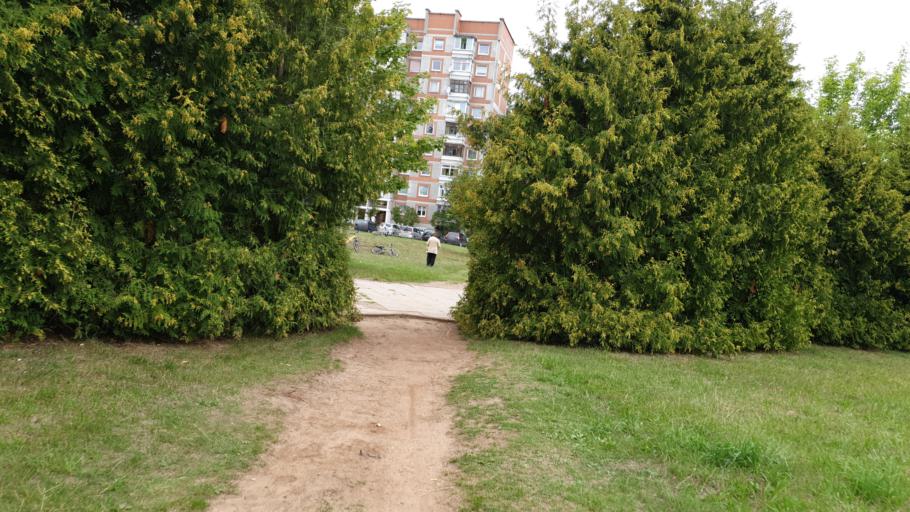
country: LT
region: Utenos apskritis
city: Visaginas
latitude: 55.5932
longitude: 26.4452
